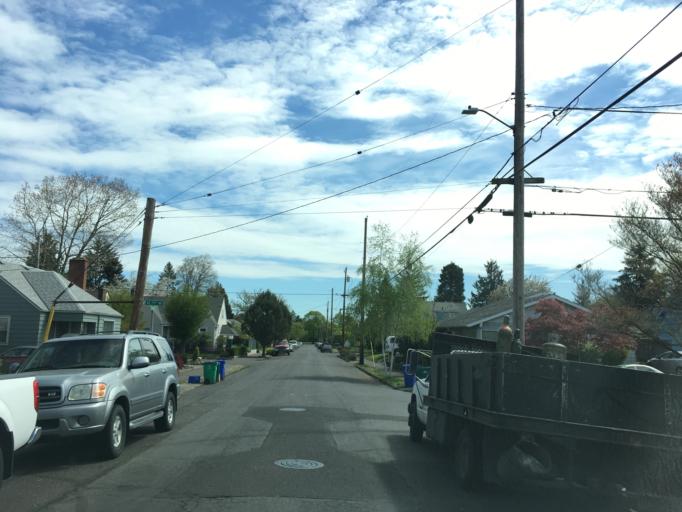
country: US
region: Oregon
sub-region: Multnomah County
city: Lents
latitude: 45.5284
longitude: -122.5828
